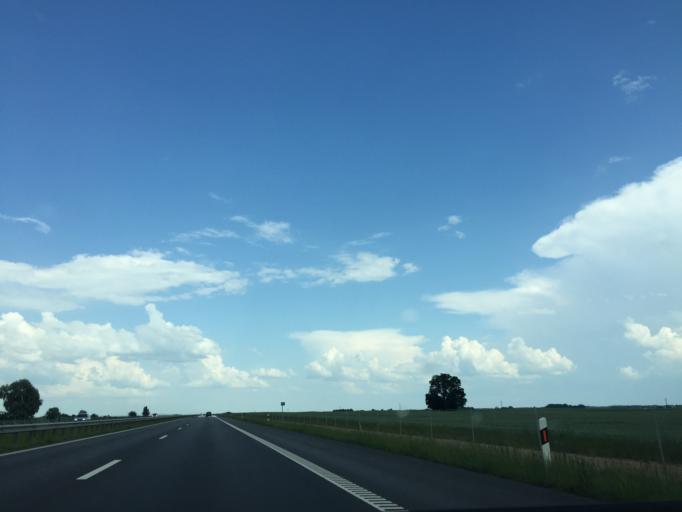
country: LT
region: Marijampoles apskritis
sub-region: Marijampole Municipality
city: Marijampole
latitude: 54.6353
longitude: 23.4545
